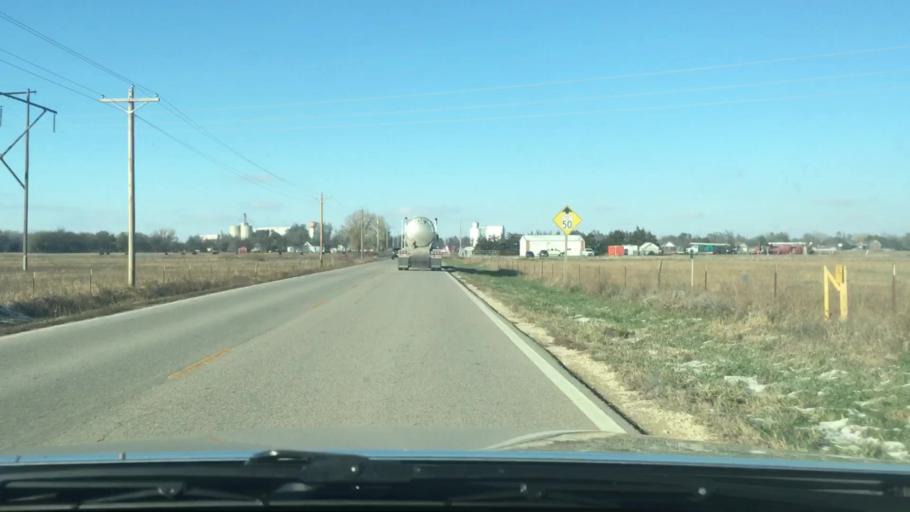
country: US
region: Kansas
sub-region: Rice County
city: Sterling
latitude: 38.1956
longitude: -98.2069
